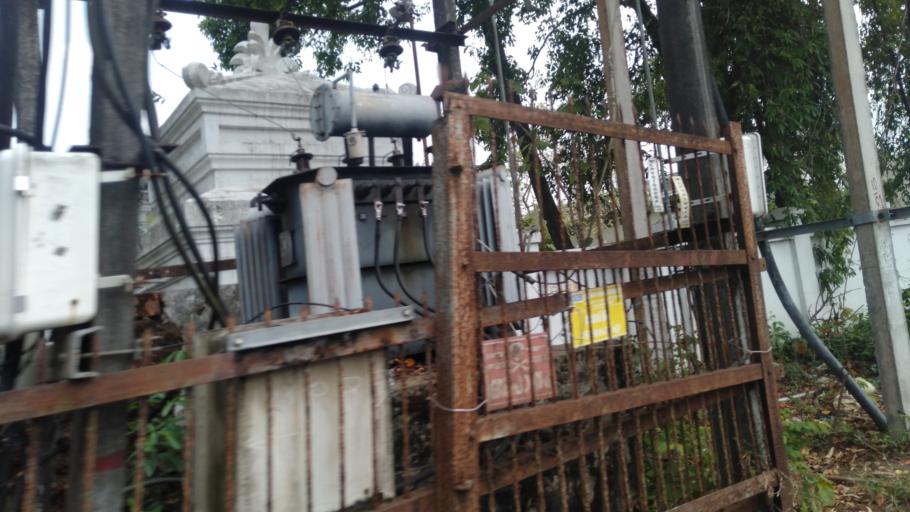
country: IN
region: Kerala
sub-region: Alappuzha
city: Alleppey
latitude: 9.4947
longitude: 76.3254
